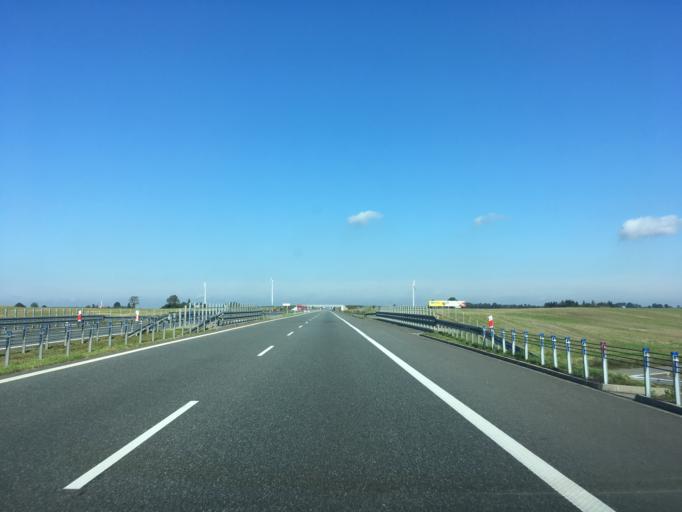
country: PL
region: Kujawsko-Pomorskie
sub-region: Powiat chelminski
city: Lisewo
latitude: 53.3638
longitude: 18.6983
